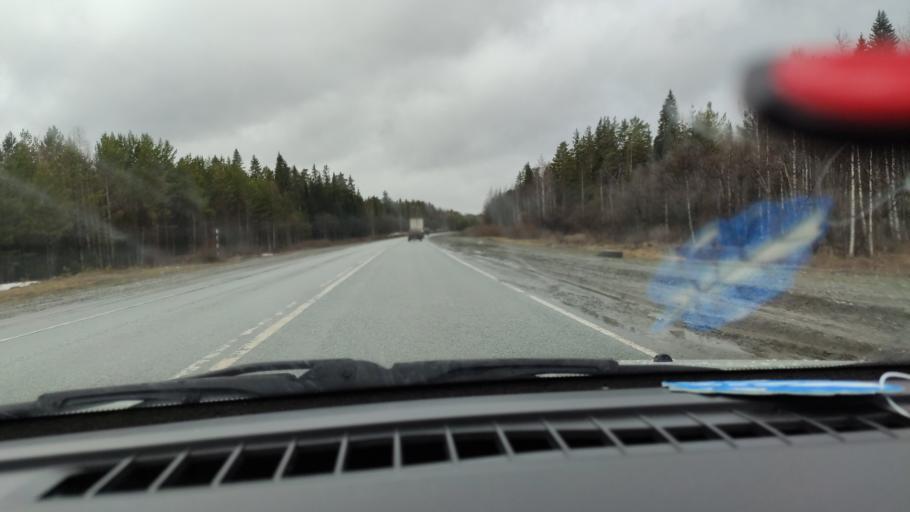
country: RU
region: Sverdlovsk
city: Atig
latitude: 56.7972
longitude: 59.3953
